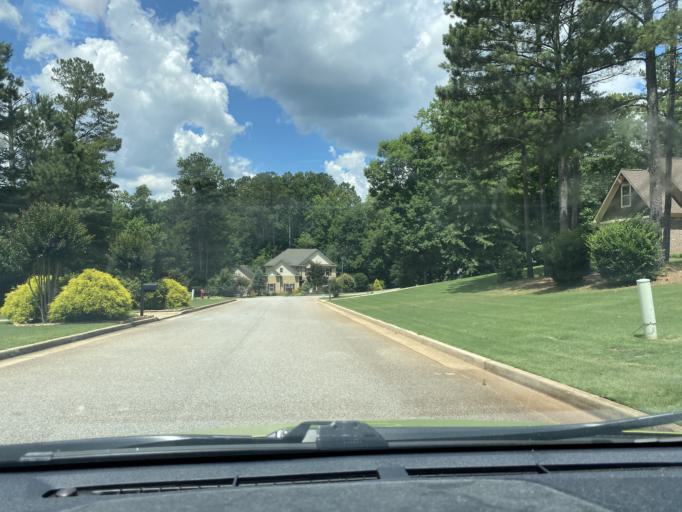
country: US
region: Georgia
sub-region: Fayette County
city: Peachtree City
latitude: 33.4299
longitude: -84.6770
